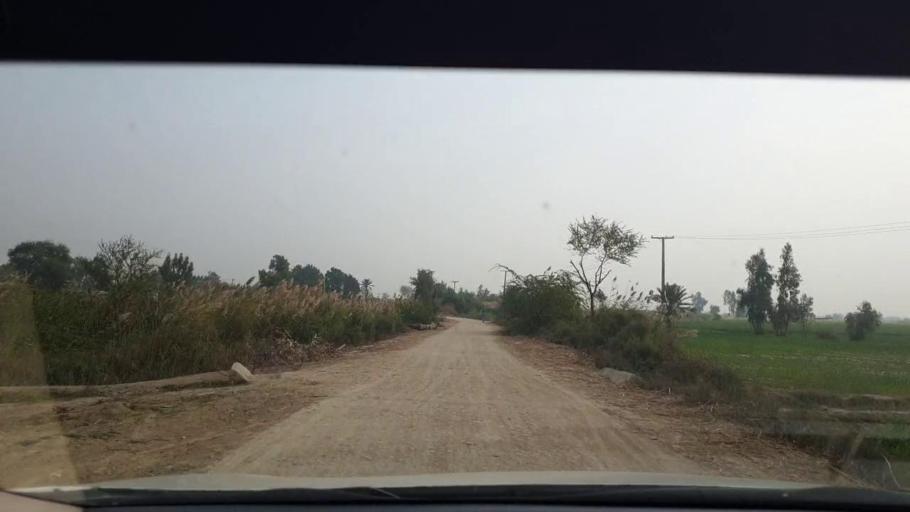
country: PK
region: Sindh
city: Berani
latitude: 25.8328
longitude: 68.8291
